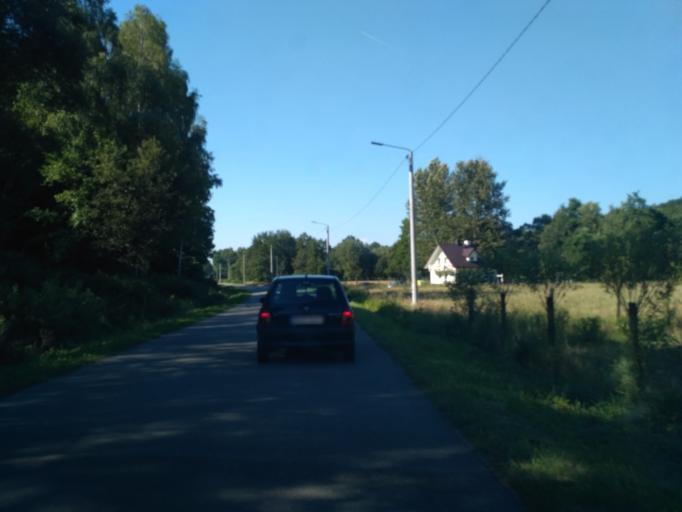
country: PL
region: Subcarpathian Voivodeship
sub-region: Powiat strzyzowski
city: Wysoka Strzyzowska
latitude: 49.7880
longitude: 21.7581
